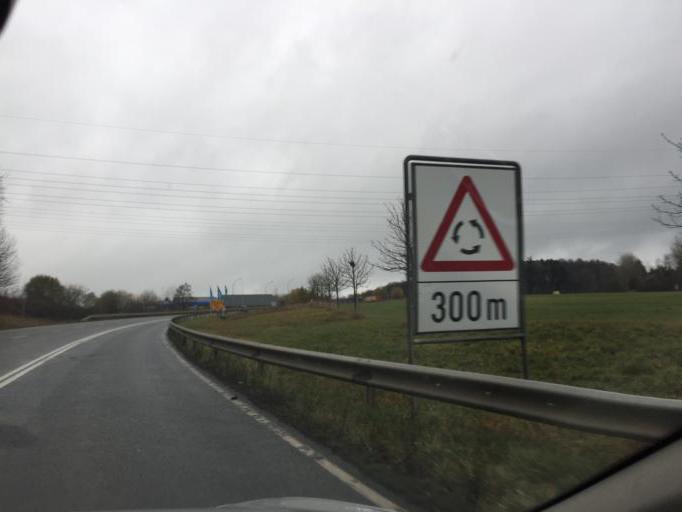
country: LU
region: Diekirch
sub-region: Canton de Diekirch
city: Diekirch
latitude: 49.8841
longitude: 6.1408
